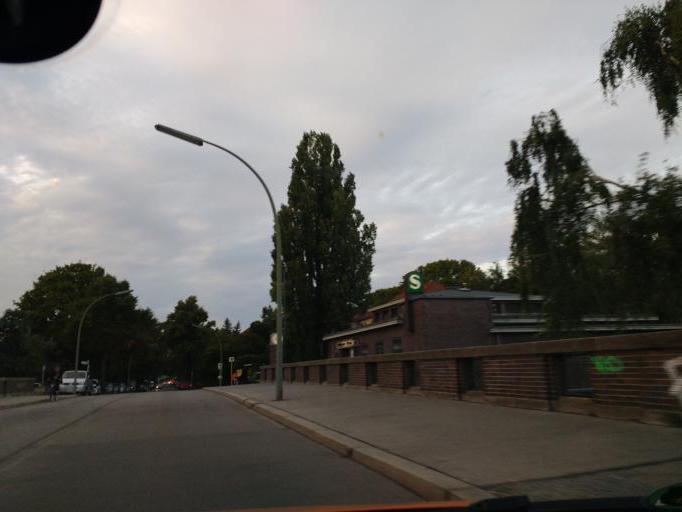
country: DE
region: Berlin
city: Zehlendorf Bezirk
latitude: 52.4359
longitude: 13.2737
